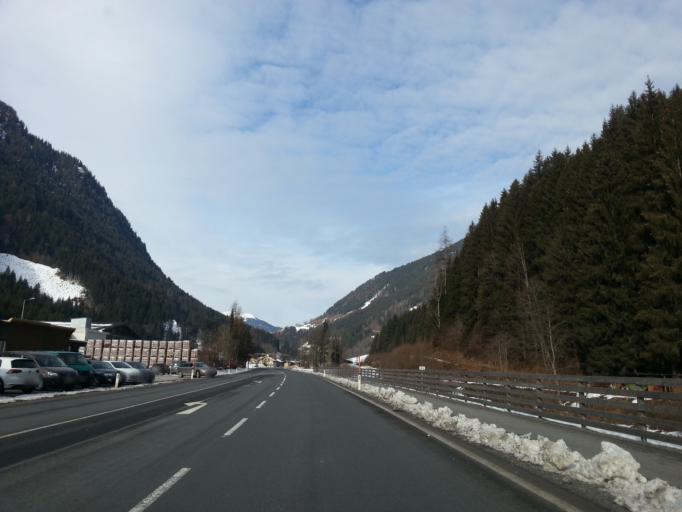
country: AT
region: Salzburg
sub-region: Politischer Bezirk Zell am See
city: Maishofen
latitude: 47.3633
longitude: 12.7913
